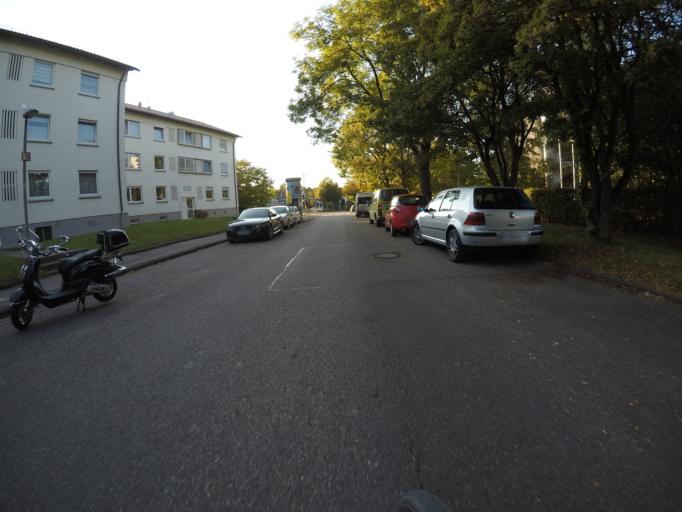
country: DE
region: Baden-Wuerttemberg
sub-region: Regierungsbezirk Stuttgart
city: Ostfildern
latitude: 48.7405
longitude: 9.2285
